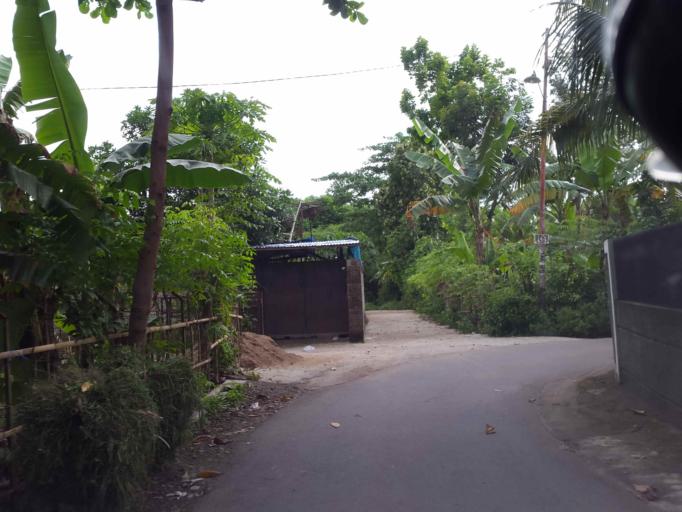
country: ID
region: West Nusa Tenggara
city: Mambalan
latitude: -8.5443
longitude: 116.0882
